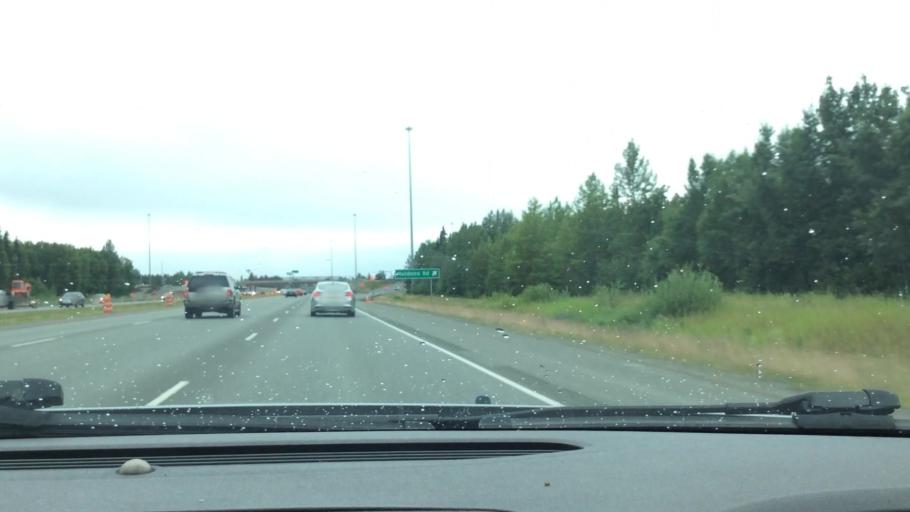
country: US
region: Alaska
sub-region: Anchorage Municipality
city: Elmendorf Air Force Base
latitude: 61.2297
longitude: -149.7221
